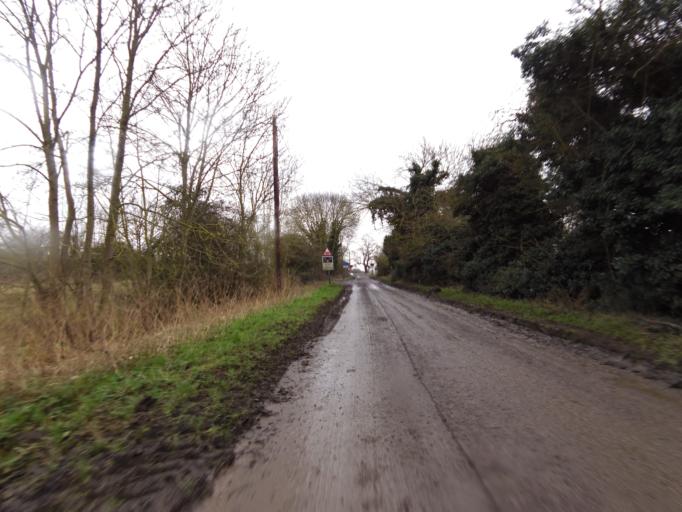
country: GB
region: England
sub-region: Cambridgeshire
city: Waterbeach
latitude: 52.2400
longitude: 0.1717
